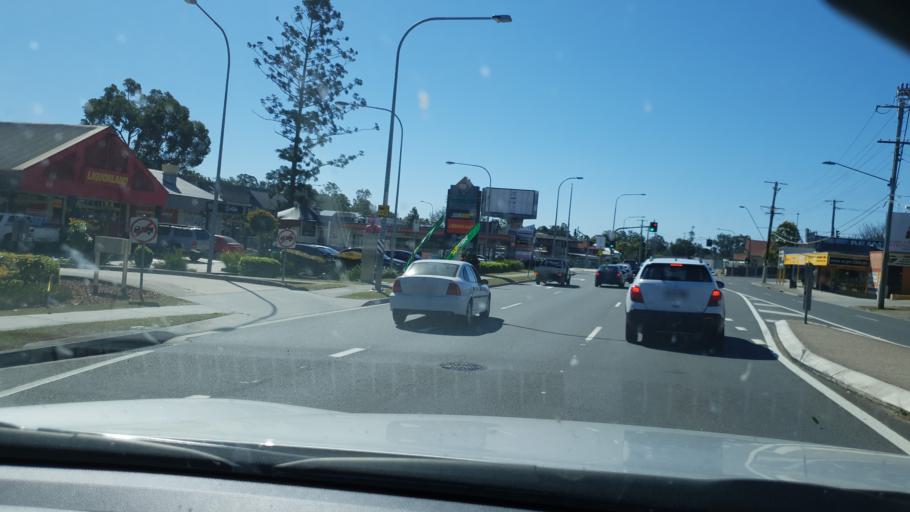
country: AU
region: Queensland
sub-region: Brisbane
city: Everton Park
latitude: -27.4235
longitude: 152.9905
